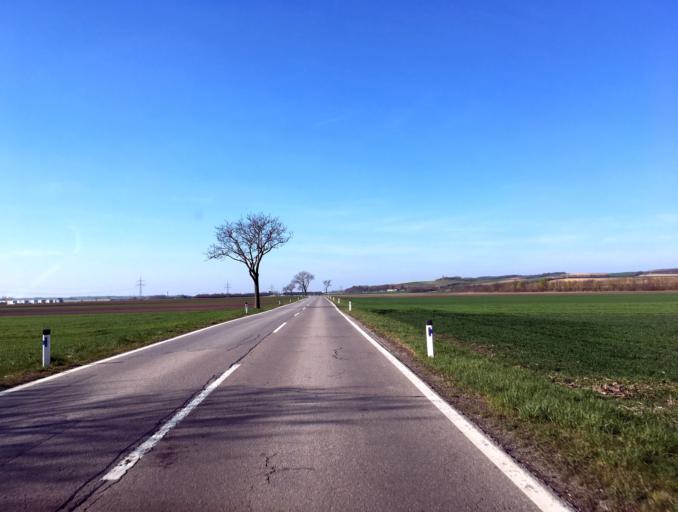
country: AT
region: Lower Austria
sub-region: Politischer Bezirk Bruck an der Leitha
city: Trautmannsdorf an der Leitha
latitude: 48.0449
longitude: 16.6214
